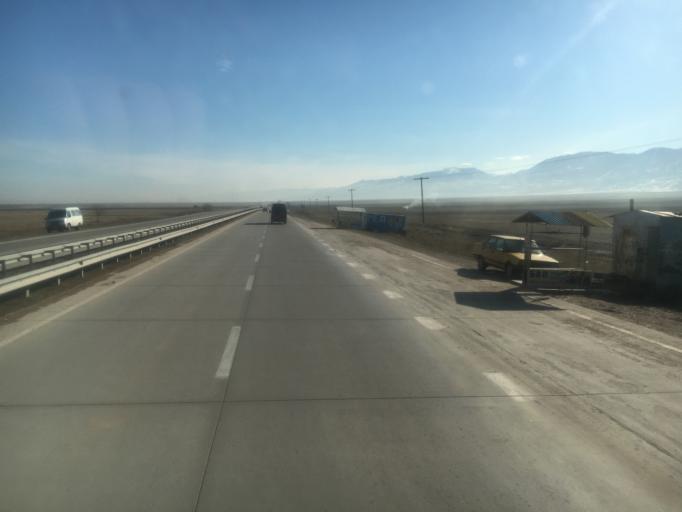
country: KZ
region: Zhambyl
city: Lugovoy
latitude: 42.9052
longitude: 72.9136
